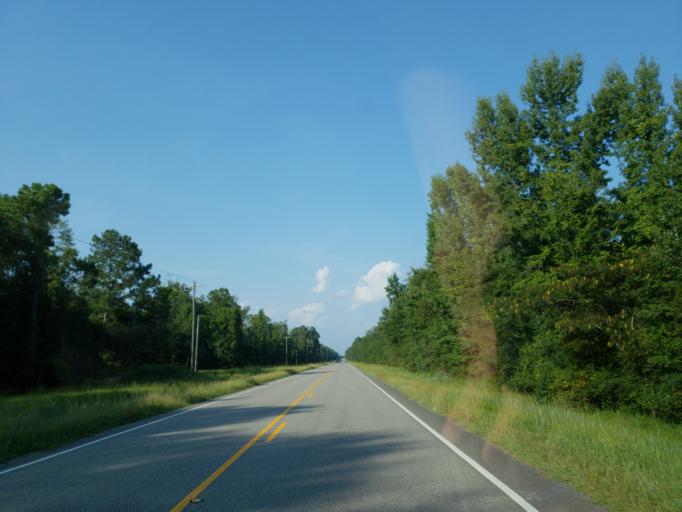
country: US
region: Alabama
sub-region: Sumter County
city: Livingston
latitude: 32.7294
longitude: -88.0620
